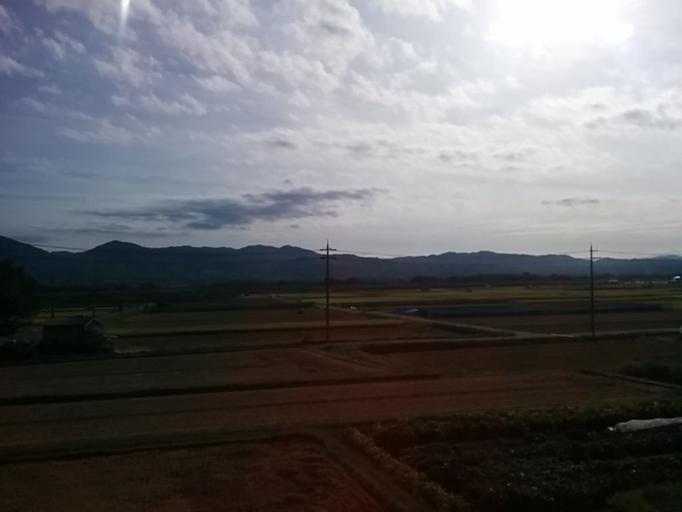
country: JP
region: Kyoto
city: Tanabe
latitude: 34.7940
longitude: 135.7871
